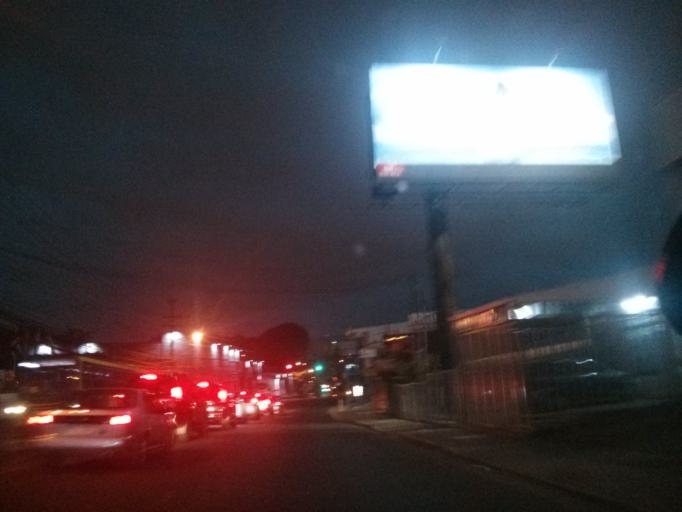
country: CR
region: San Jose
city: Colima
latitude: 9.9468
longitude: -84.0898
